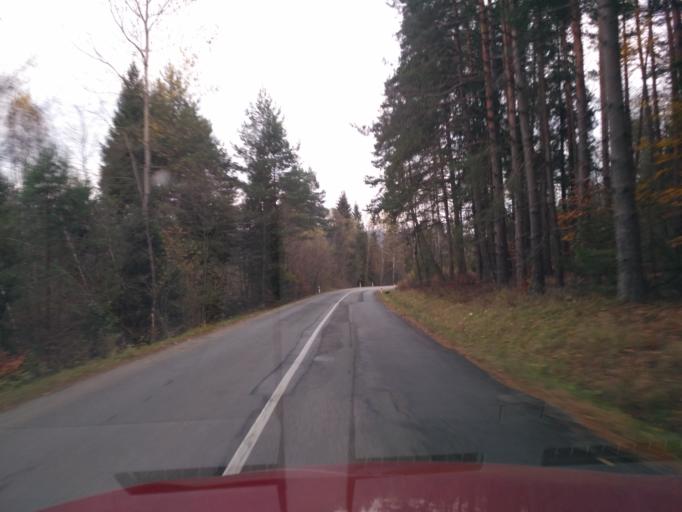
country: SK
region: Kosicky
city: Medzev
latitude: 48.7937
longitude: 20.7825
